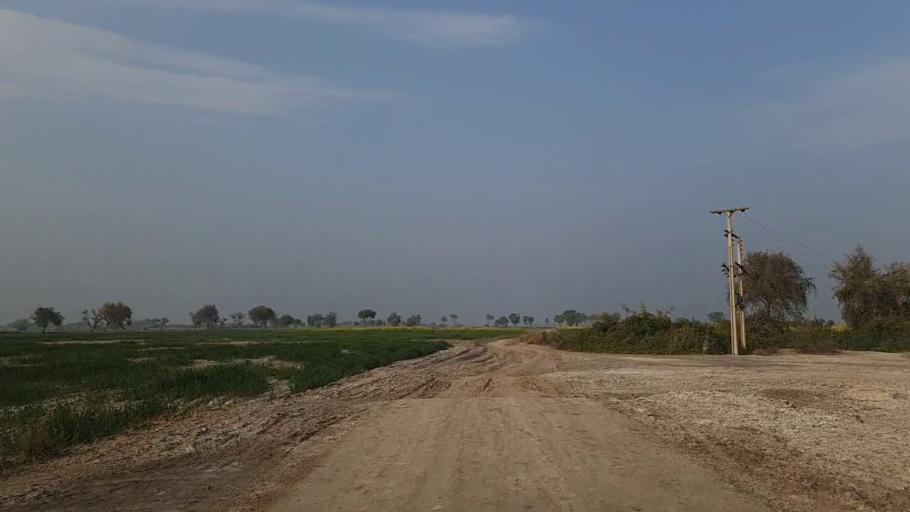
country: PK
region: Sindh
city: Jam Sahib
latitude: 26.3074
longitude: 68.5168
